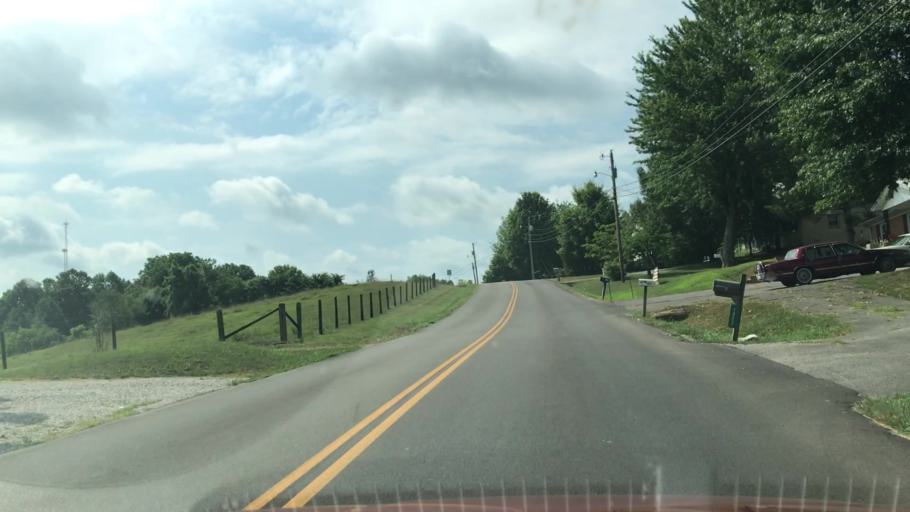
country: US
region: Kentucky
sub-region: Barren County
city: Glasgow
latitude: 36.9832
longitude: -85.9034
